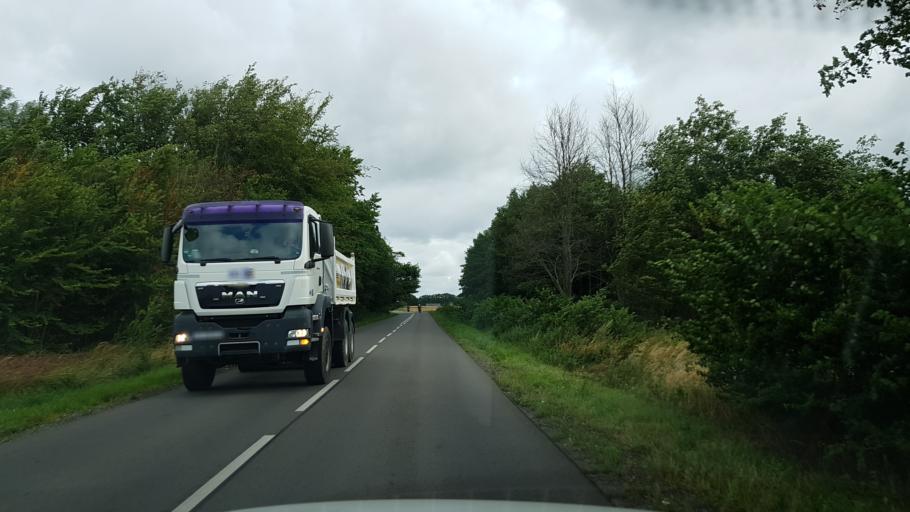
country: PL
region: West Pomeranian Voivodeship
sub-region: Powiat gryficki
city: Rewal
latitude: 54.0640
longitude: 15.0273
